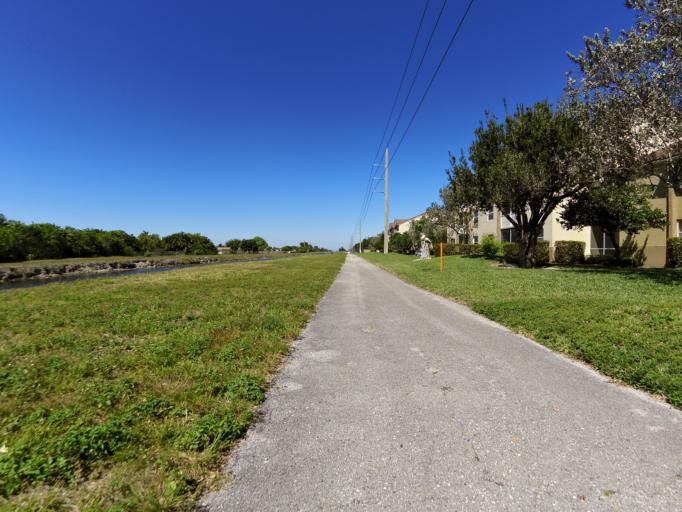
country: US
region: Florida
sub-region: Broward County
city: Tamarac
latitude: 26.1747
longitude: -80.2978
